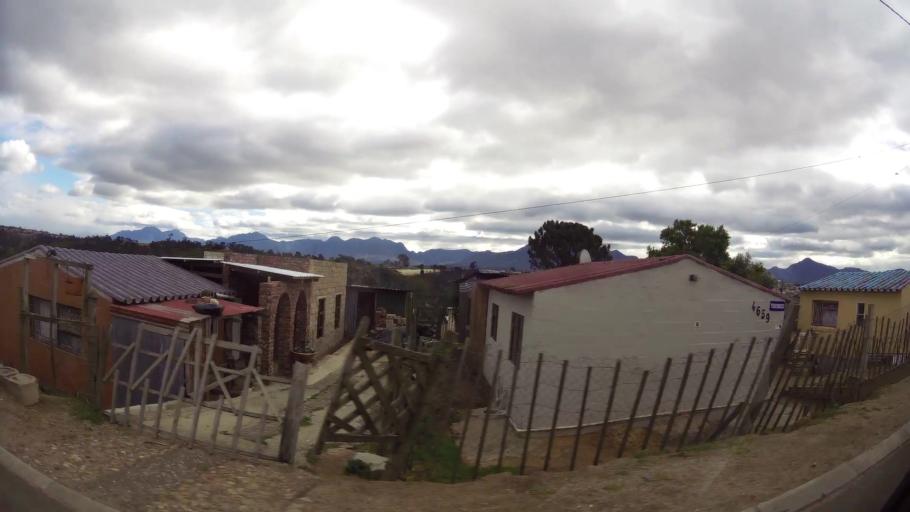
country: ZA
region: Western Cape
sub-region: Eden District Municipality
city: George
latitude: -34.0141
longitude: 22.4763
